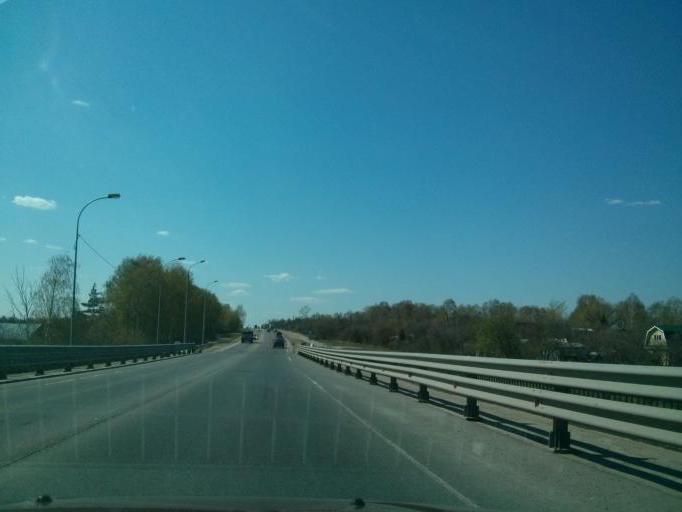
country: RU
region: Nizjnij Novgorod
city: Burevestnik
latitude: 56.1829
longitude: 43.8067
